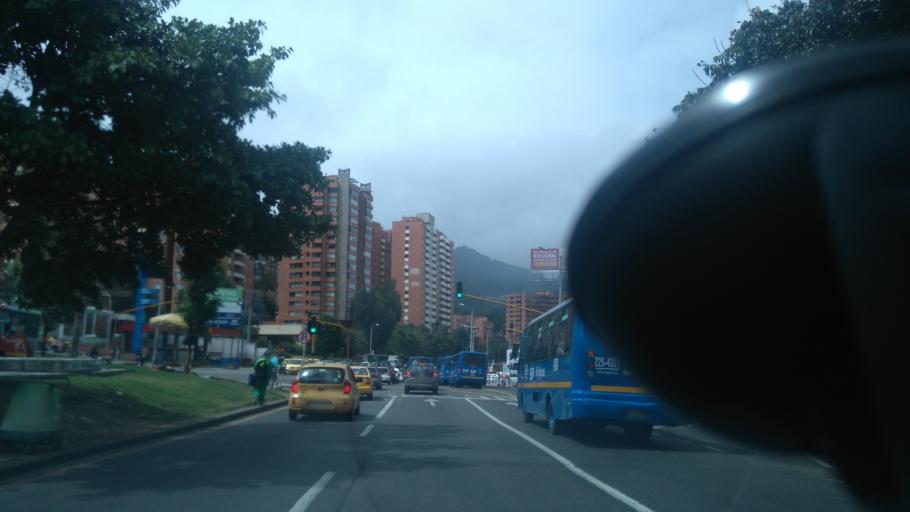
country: CO
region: Bogota D.C.
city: Barrio San Luis
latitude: 4.7027
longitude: -74.0287
